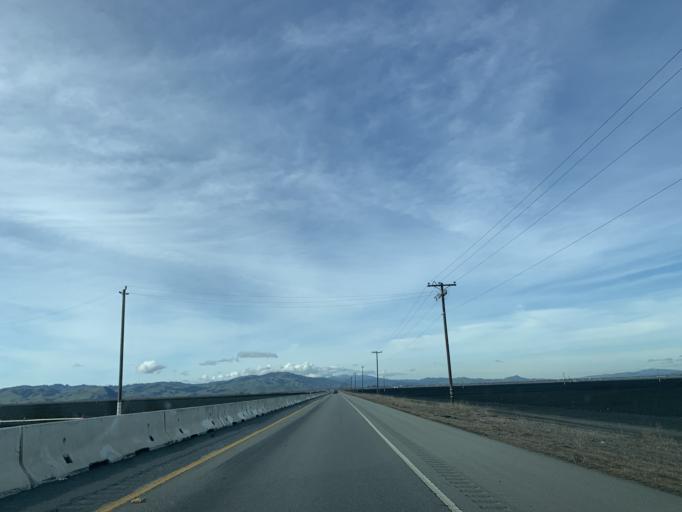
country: US
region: California
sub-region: San Benito County
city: Hollister
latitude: 36.9225
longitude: -121.4574
